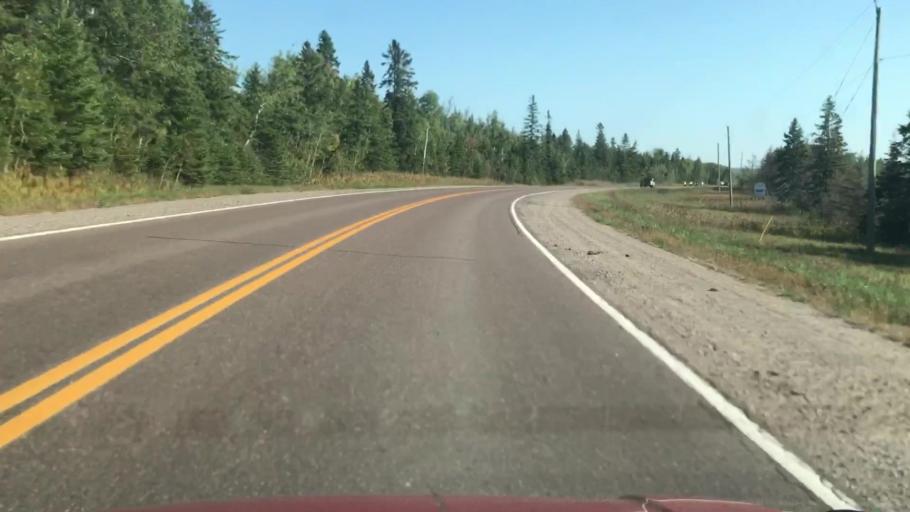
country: CA
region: Ontario
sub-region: Algoma
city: Sault Ste. Marie
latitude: 46.3349
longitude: -84.0061
